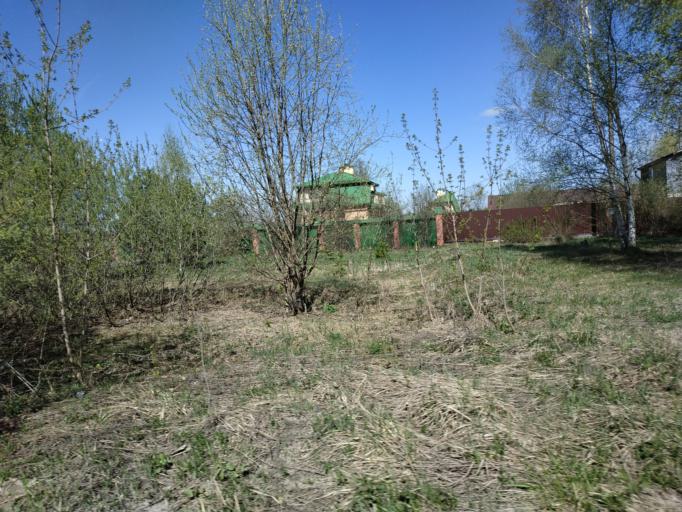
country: RU
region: Moskovskaya
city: Malyshevo
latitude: 55.4625
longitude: 38.3597
